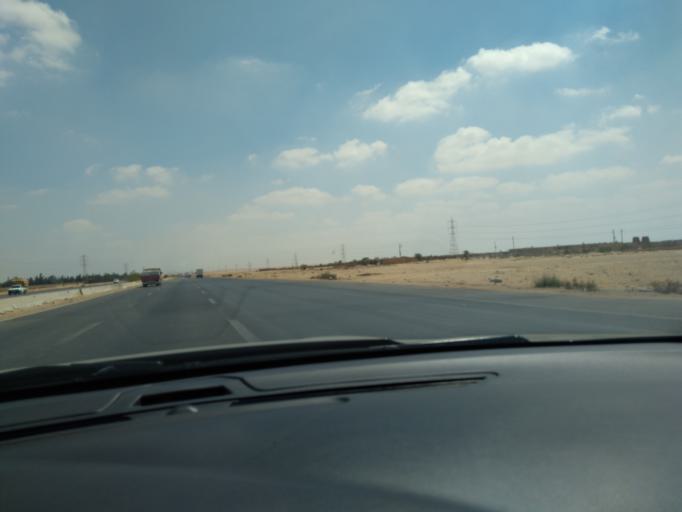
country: EG
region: Al Isma'iliyah
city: At Tall al Kabir
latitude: 30.3541
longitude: 31.8920
